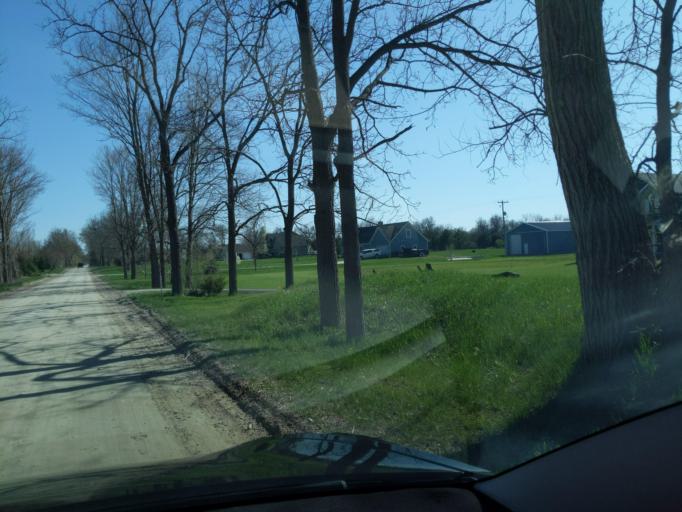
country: US
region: Michigan
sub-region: Ingham County
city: Stockbridge
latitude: 42.4203
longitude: -84.0836
